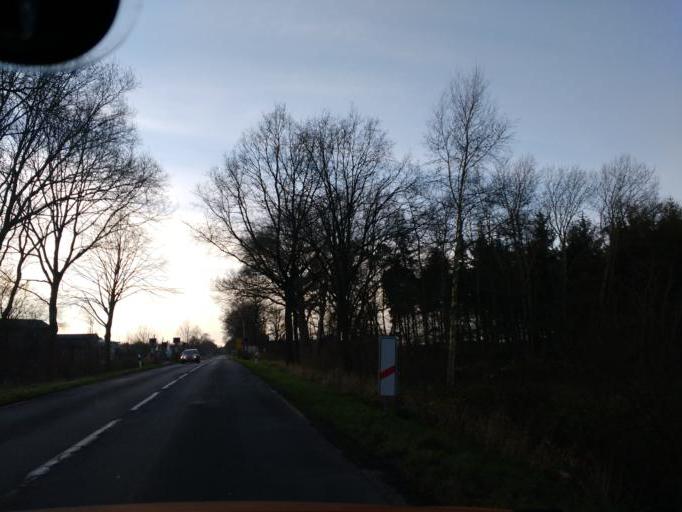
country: DE
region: Lower Saxony
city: Hude
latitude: 53.1130
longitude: 8.4422
